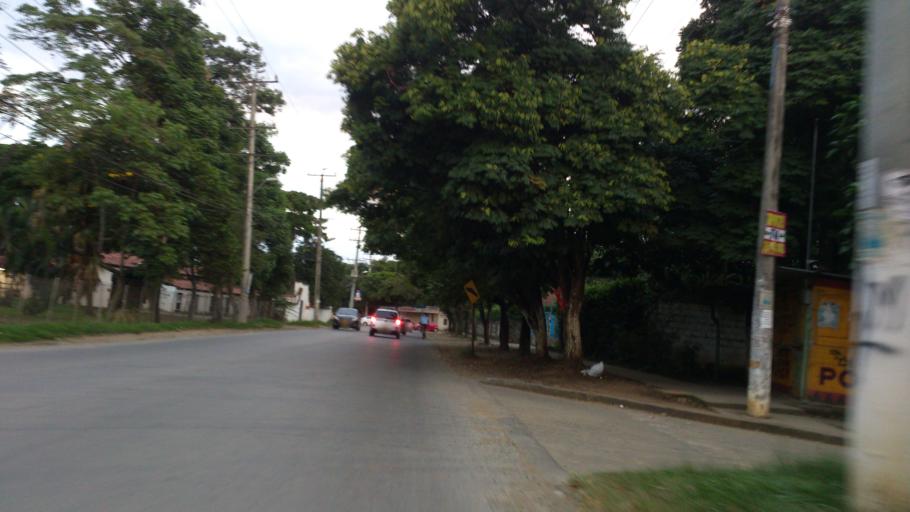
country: CO
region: Valle del Cauca
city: Jamundi
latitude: 3.2568
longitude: -76.5480
